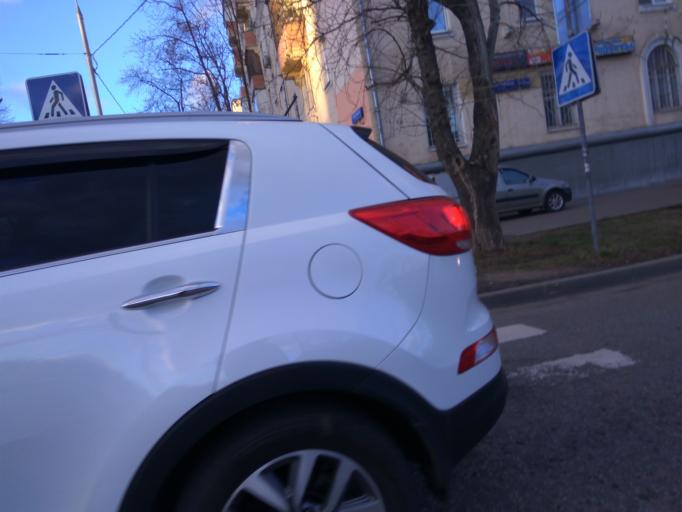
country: RU
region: Moskovskaya
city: Bogorodskoye
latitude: 55.8185
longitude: 37.7218
